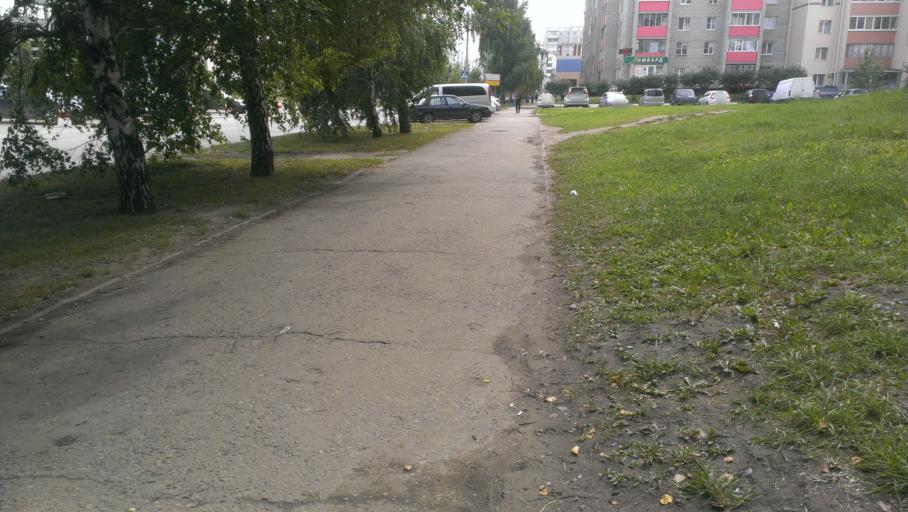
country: RU
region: Altai Krai
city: Novosilikatnyy
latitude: 53.3378
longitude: 83.6775
